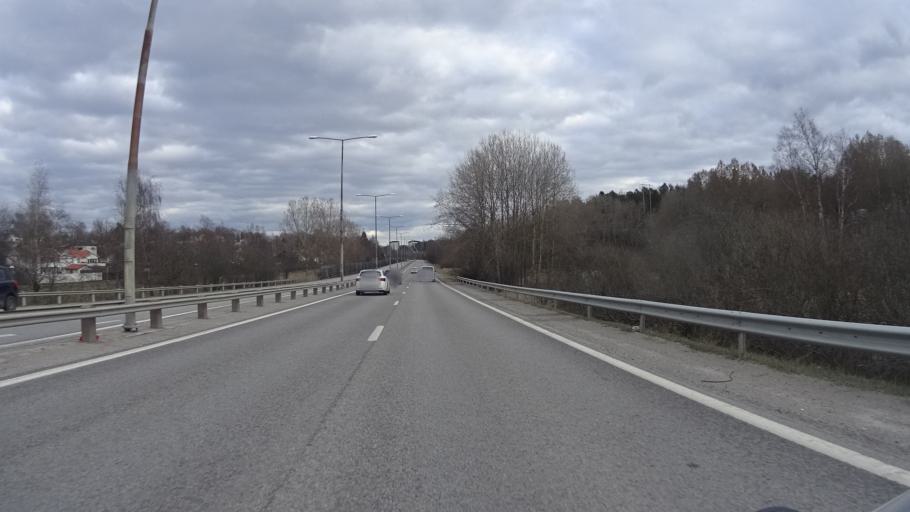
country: SE
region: Stockholm
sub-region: Stockholms Kommun
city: Arsta
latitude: 59.2709
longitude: 18.0163
